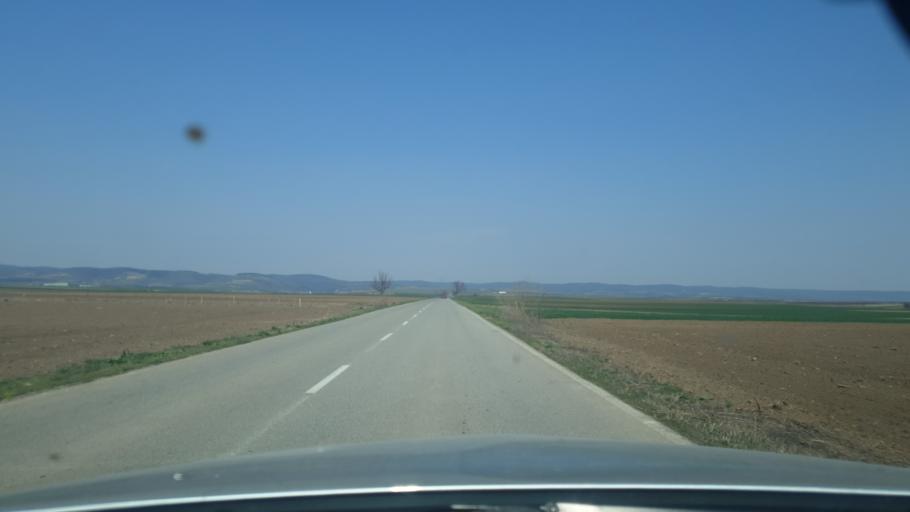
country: RS
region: Autonomna Pokrajina Vojvodina
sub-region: Sremski Okrug
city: Ruma
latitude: 45.0534
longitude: 19.7657
